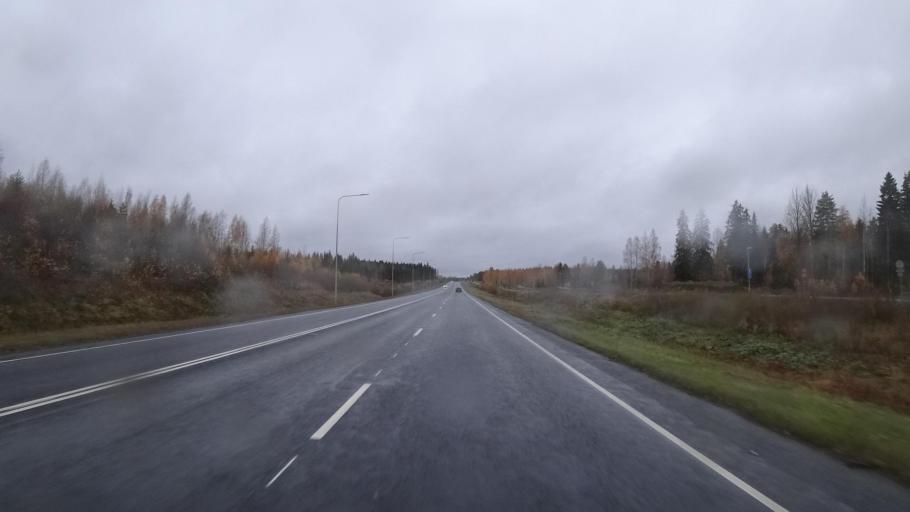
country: FI
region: Northern Savo
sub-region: Kuopio
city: Kuopio
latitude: 62.9761
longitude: 27.8062
